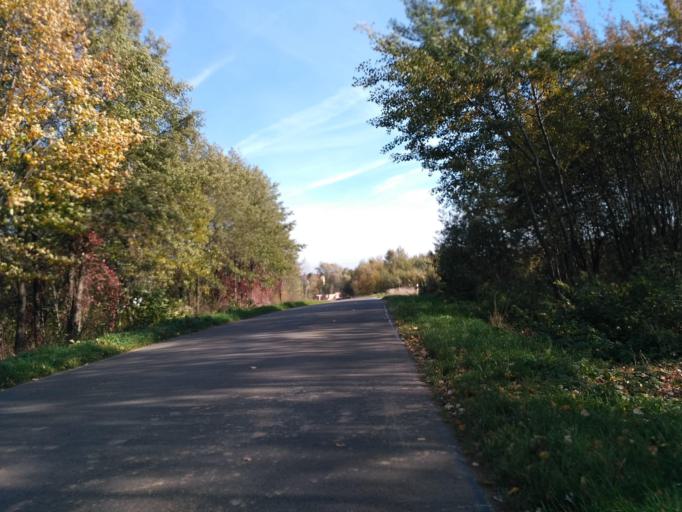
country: PL
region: Subcarpathian Voivodeship
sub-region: Powiat ropczycko-sedziszowski
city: Iwierzyce
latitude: 50.0527
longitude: 21.7703
